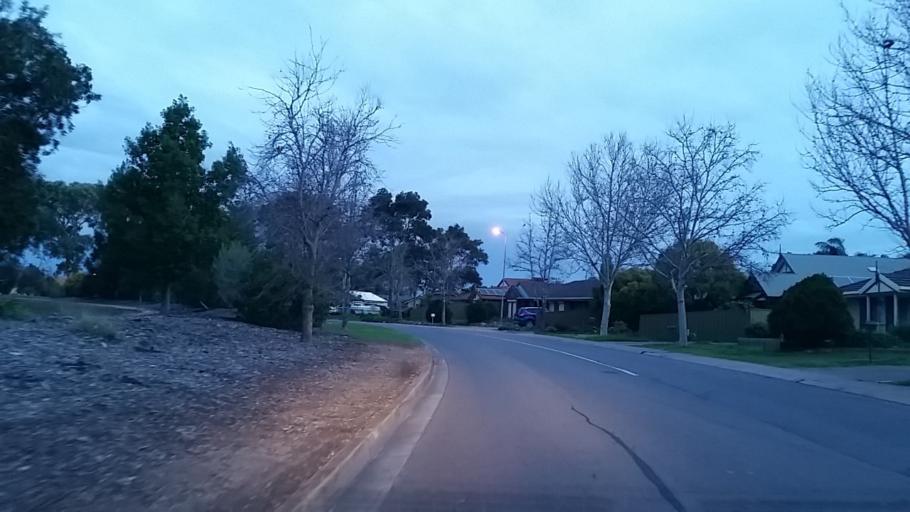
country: AU
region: South Australia
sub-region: Playford
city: Smithfield
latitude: -34.6703
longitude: 138.6634
